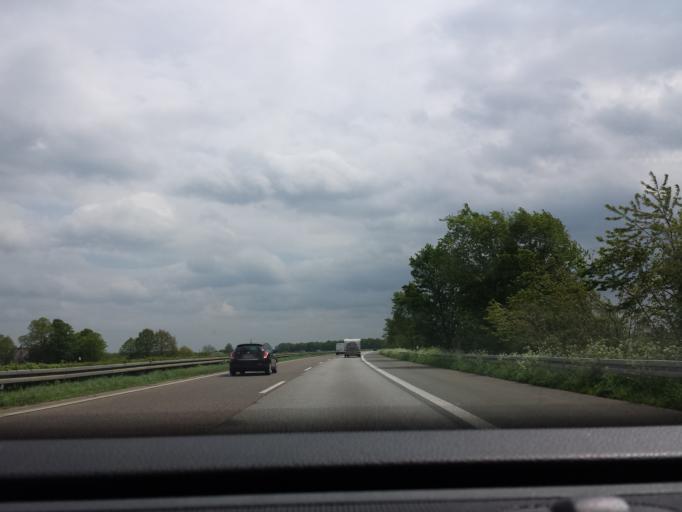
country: NL
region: Gelderland
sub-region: Gemeente Montferland
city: s-Heerenberg
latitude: 51.8600
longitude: 6.2727
